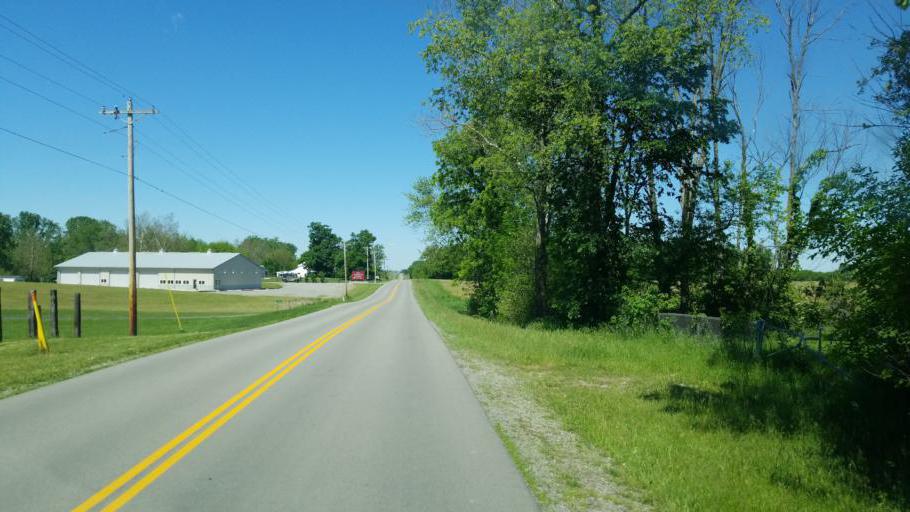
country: US
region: Ohio
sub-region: Logan County
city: Bellefontaine
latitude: 40.4286
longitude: -83.8080
